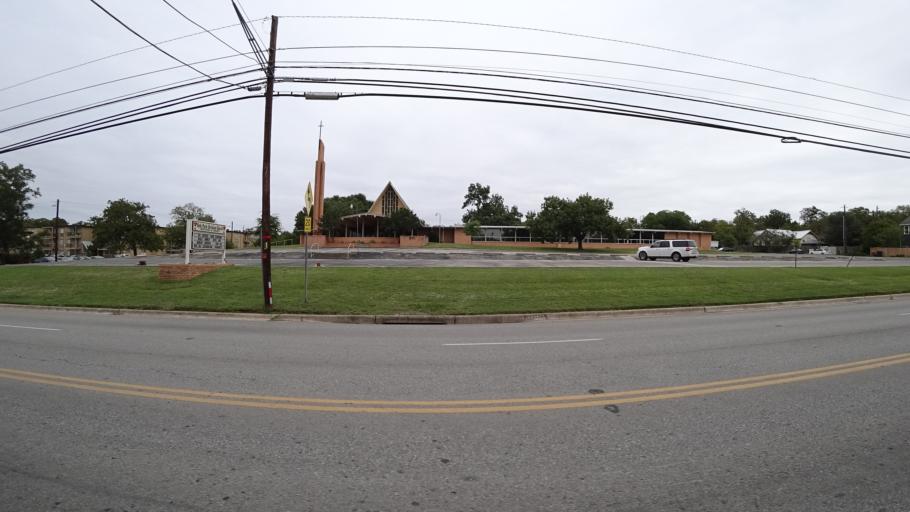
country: US
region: Texas
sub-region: Travis County
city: Austin
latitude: 30.3063
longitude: -97.7228
